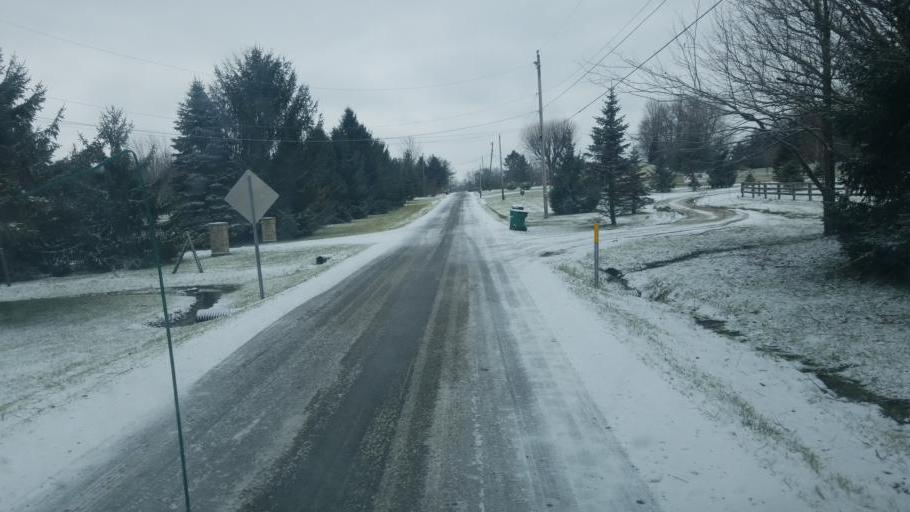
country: US
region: Ohio
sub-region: Delaware County
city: Sunbury
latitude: 40.2455
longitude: -82.7728
